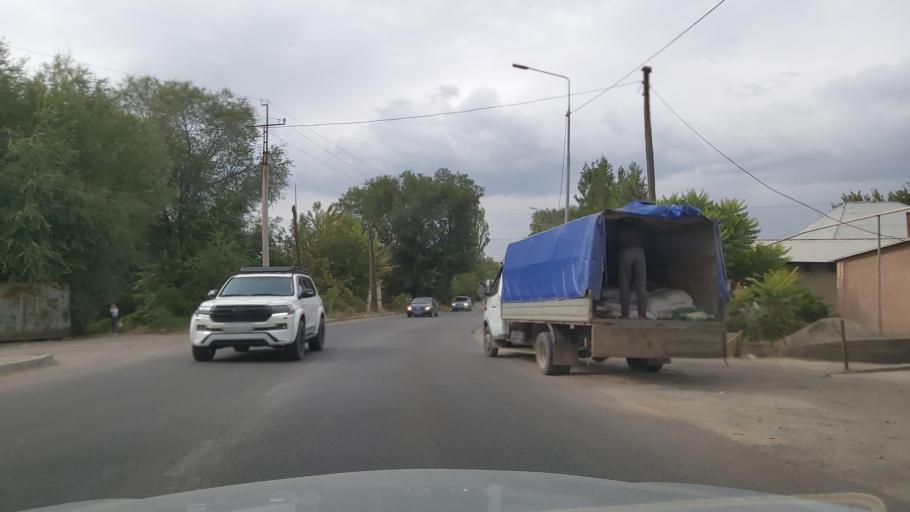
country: KZ
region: Almaty Oblysy
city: Energeticheskiy
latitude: 43.3888
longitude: 77.0744
